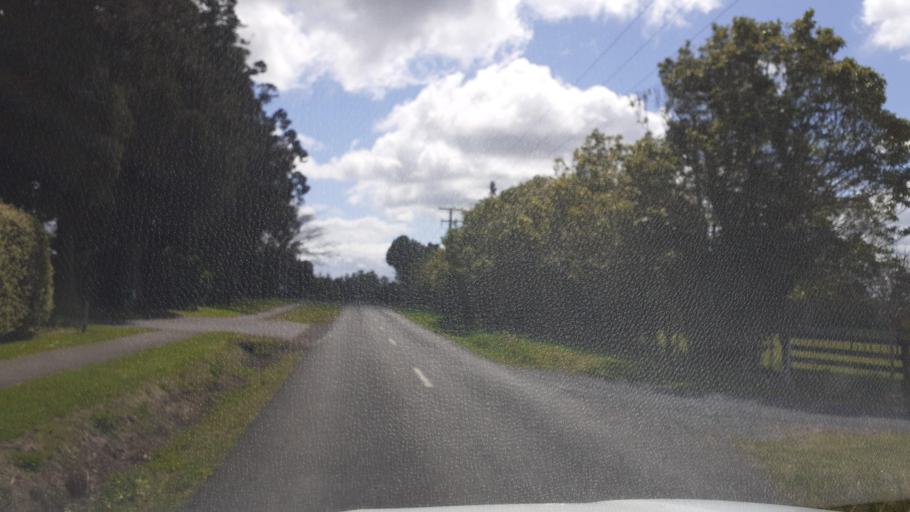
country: NZ
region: Northland
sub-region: Far North District
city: Kerikeri
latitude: -35.2428
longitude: 173.9566
